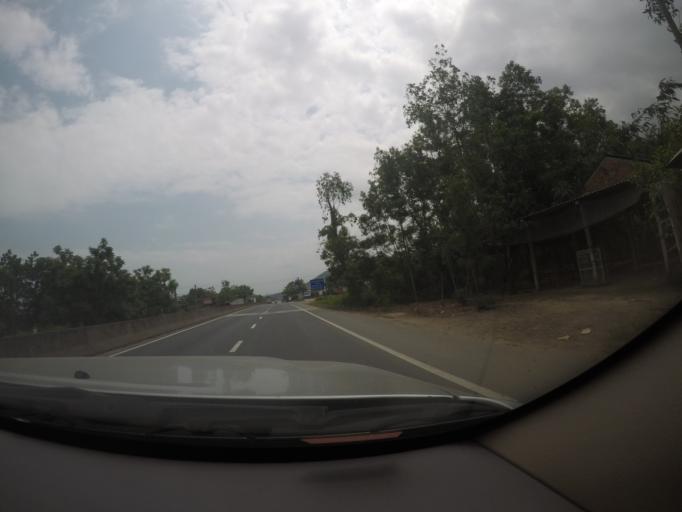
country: VN
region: Thua Thien-Hue
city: Phu Loc
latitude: 16.2886
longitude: 107.8261
